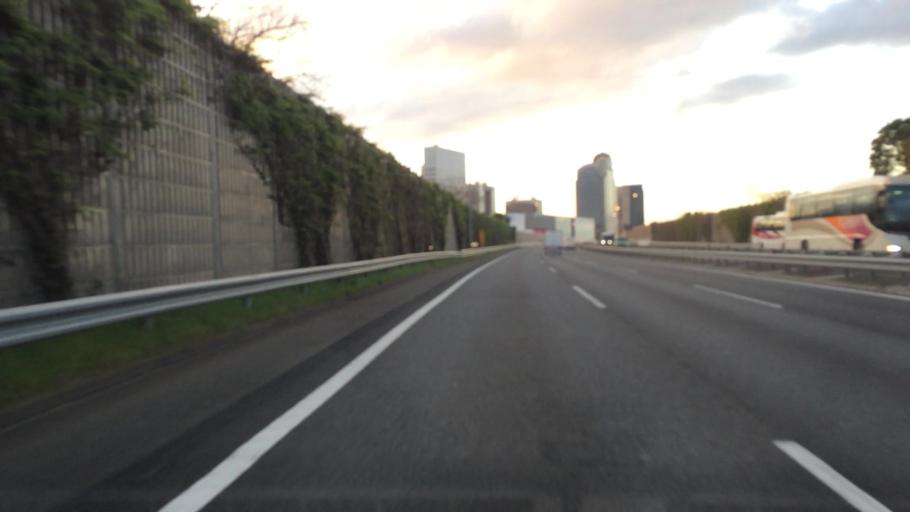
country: JP
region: Chiba
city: Funabashi
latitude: 35.6501
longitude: 140.0532
